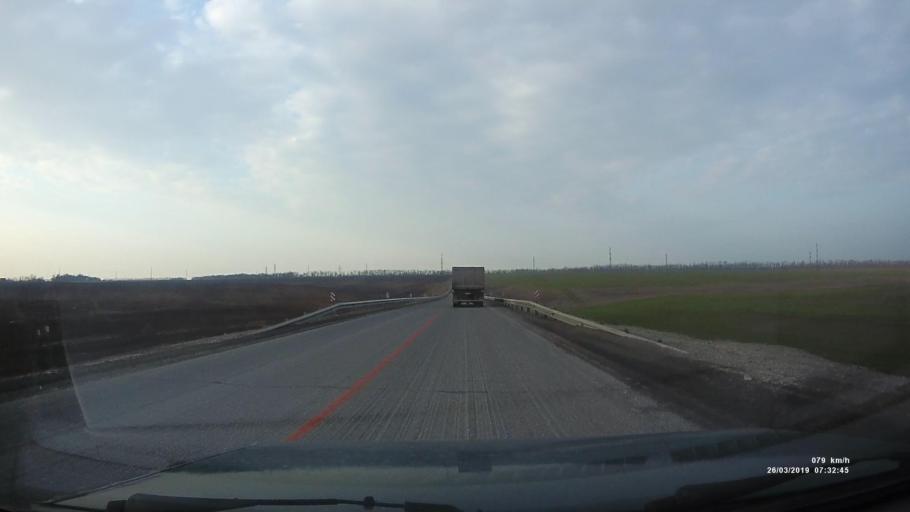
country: RU
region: Rostov
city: Novobessergenovka
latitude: 47.2220
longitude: 38.7751
